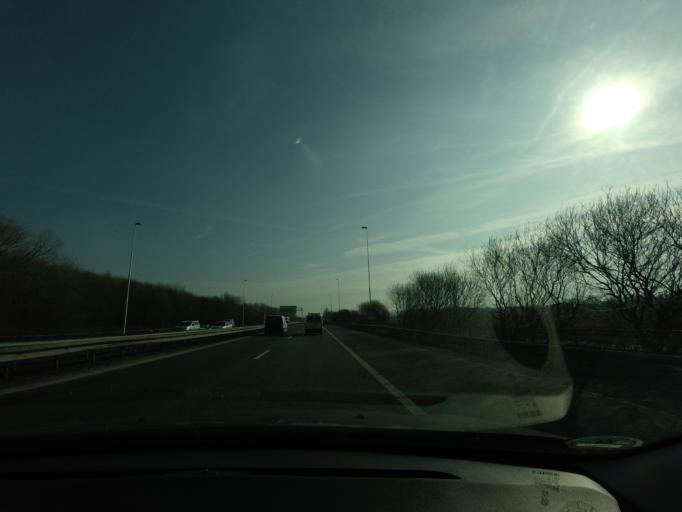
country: NL
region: North Holland
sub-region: Gemeente Velsen
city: Velsen-Zuid
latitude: 52.4339
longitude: 4.6746
